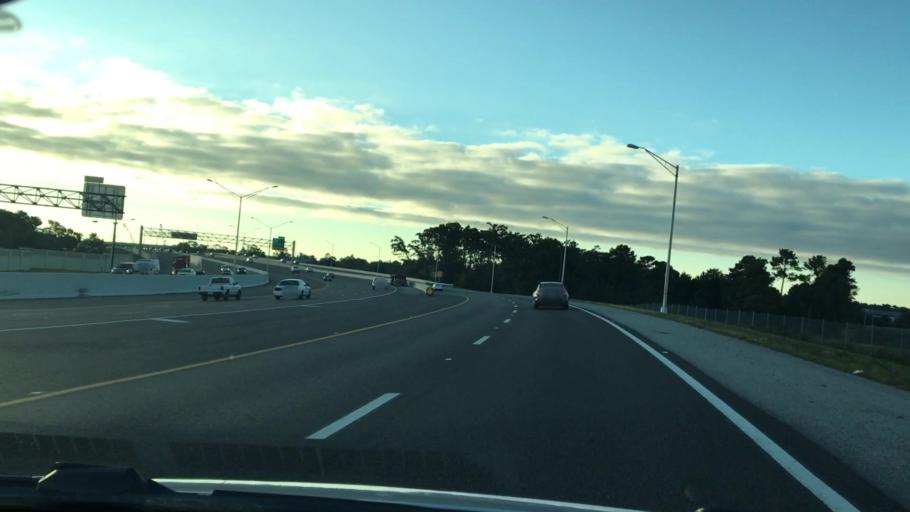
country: US
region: Florida
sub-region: Orange County
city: Union Park
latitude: 28.5578
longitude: -81.2685
